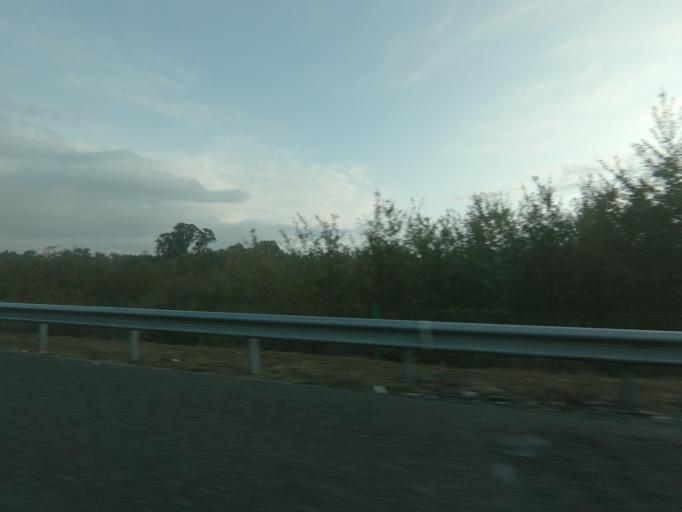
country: ES
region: Galicia
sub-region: Provincia de Pontevedra
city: Tui
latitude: 42.0877
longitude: -8.6404
